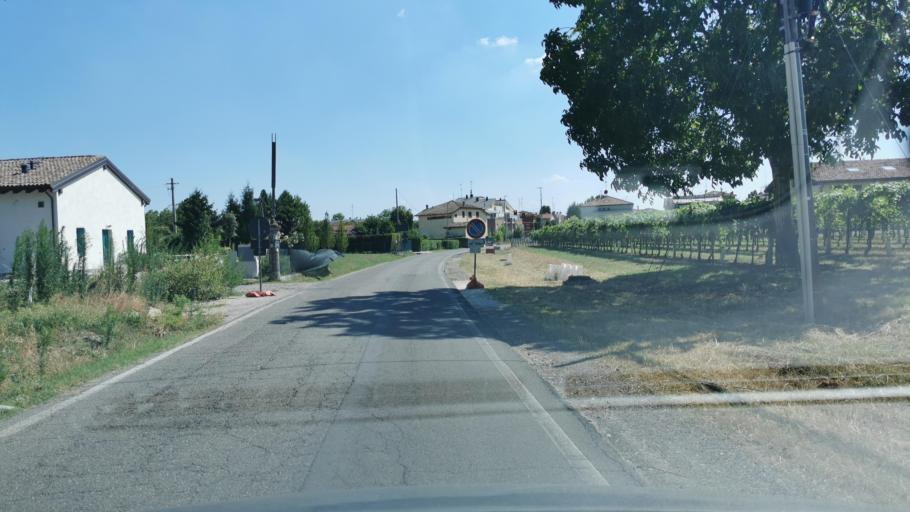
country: IT
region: Emilia-Romagna
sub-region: Provincia di Modena
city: Fossoli
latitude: 44.8206
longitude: 10.8980
